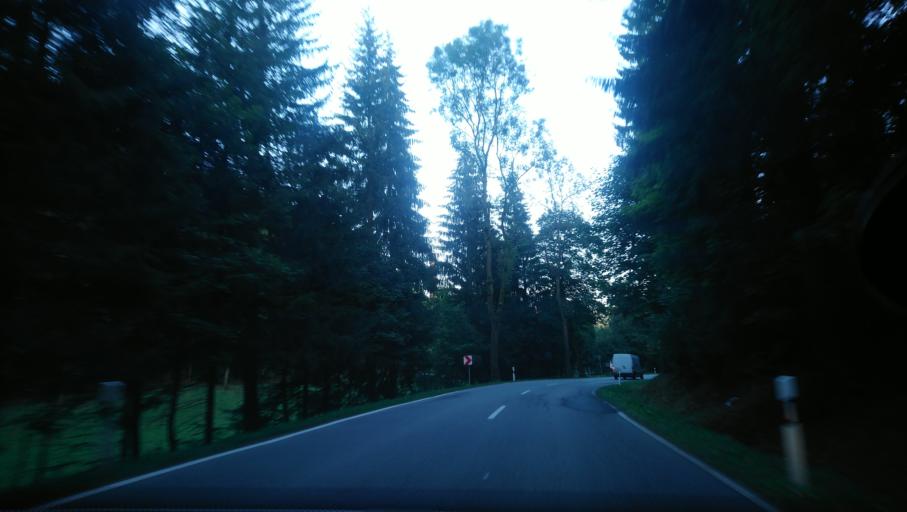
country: DE
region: Saxony
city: Tannenberg
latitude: 50.6098
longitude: 12.9328
